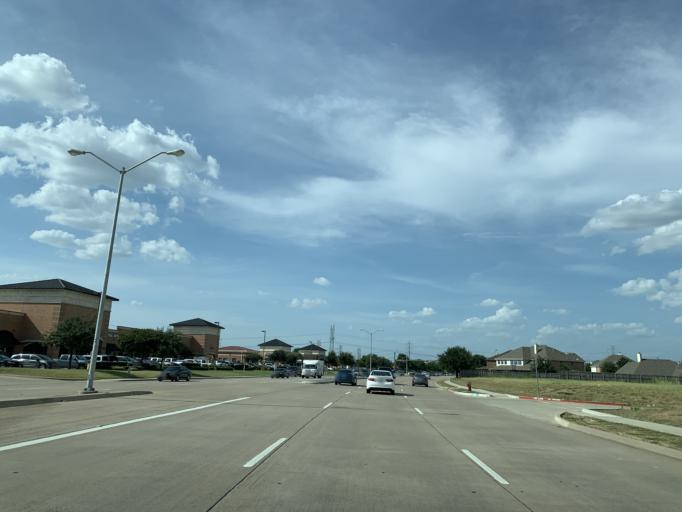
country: US
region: Texas
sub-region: Dallas County
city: Cedar Hill
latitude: 32.6494
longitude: -97.0437
